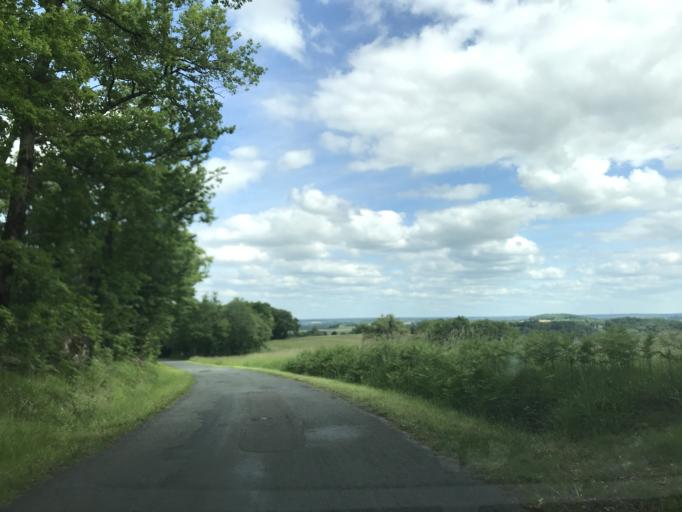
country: FR
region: Poitou-Charentes
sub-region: Departement de la Charente
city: Chalais
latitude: 45.2728
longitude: 0.1111
